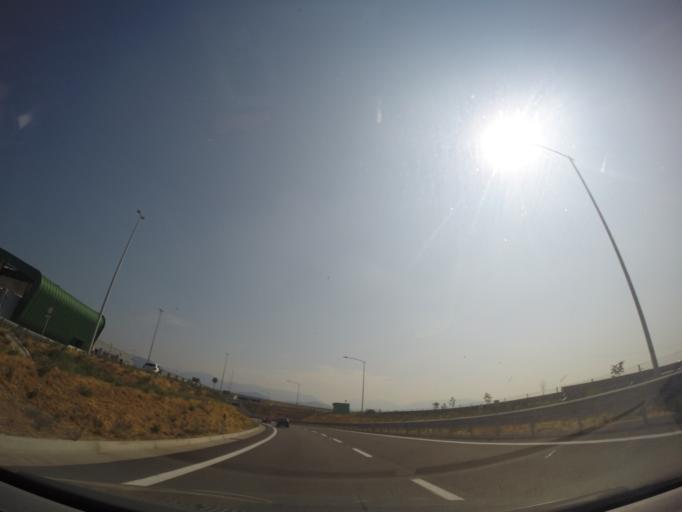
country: IT
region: Lombardy
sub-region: Provincia di Brescia
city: Castegnato
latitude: 45.5445
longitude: 10.1142
